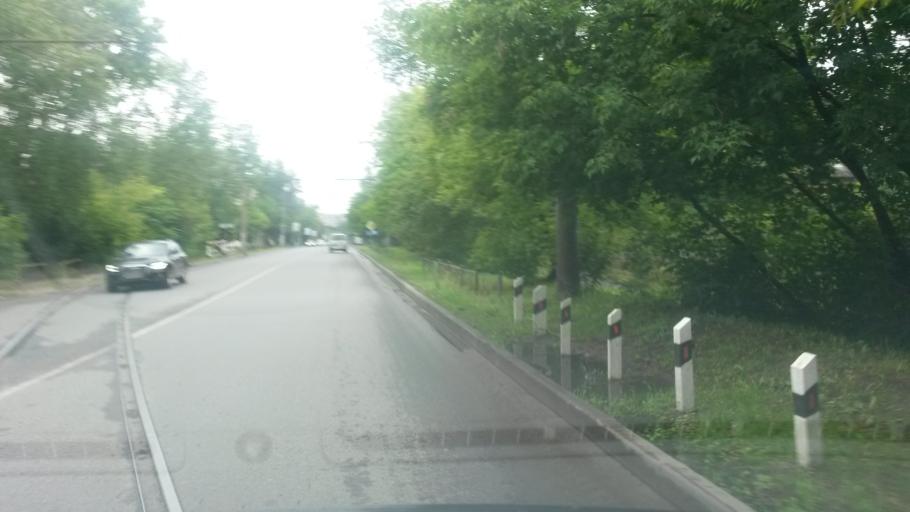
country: RU
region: Ivanovo
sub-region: Gorod Ivanovo
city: Ivanovo
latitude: 57.0089
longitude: 40.9448
